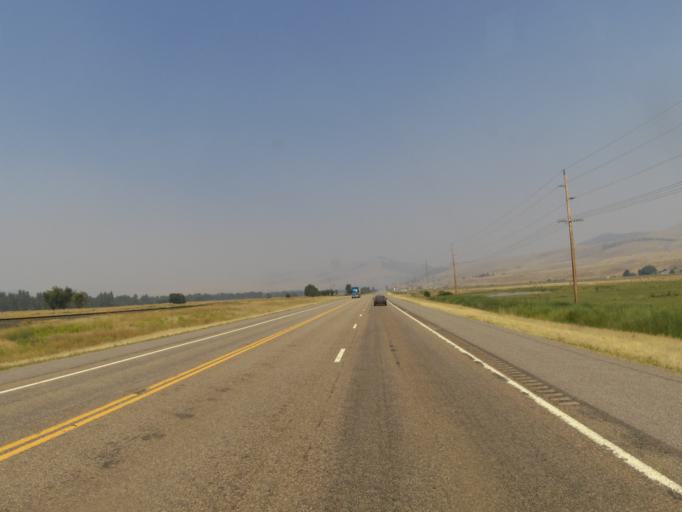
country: US
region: Montana
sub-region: Missoula County
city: Frenchtown
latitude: 47.2115
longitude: -114.1240
